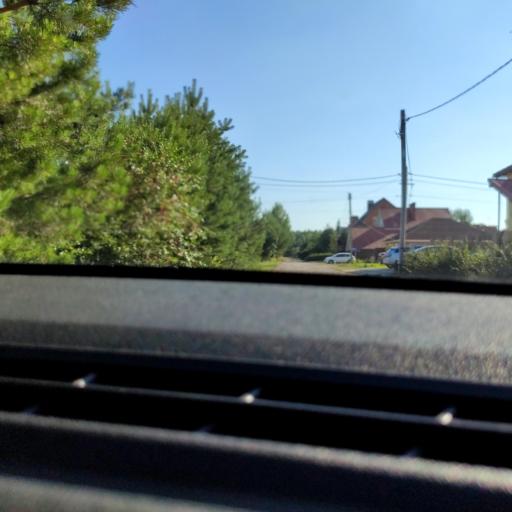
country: RU
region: Samara
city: Podstepki
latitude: 53.5707
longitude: 49.0706
